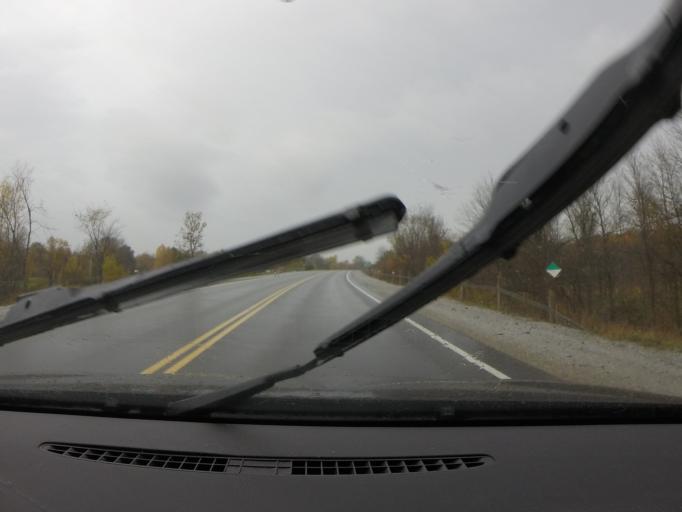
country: CA
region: Ontario
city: Perth
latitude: 44.8360
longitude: -76.5272
